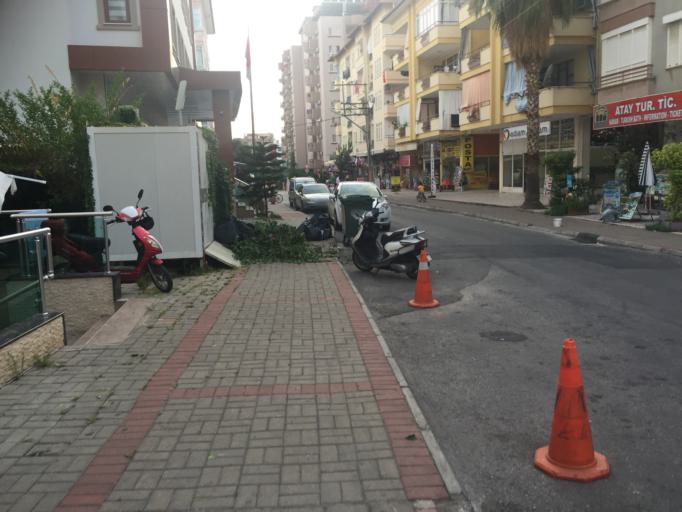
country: TR
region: Antalya
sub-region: Alanya
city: Alanya
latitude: 36.5524
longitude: 31.9858
